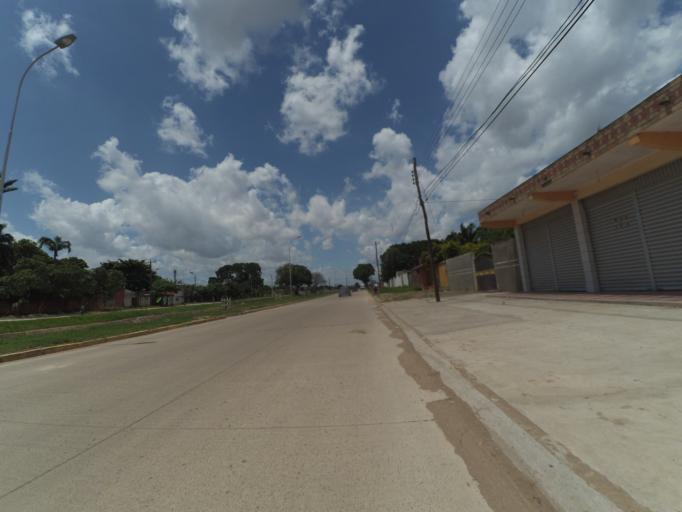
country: BO
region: Santa Cruz
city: Santa Cruz de la Sierra
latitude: -17.7294
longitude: -63.1494
